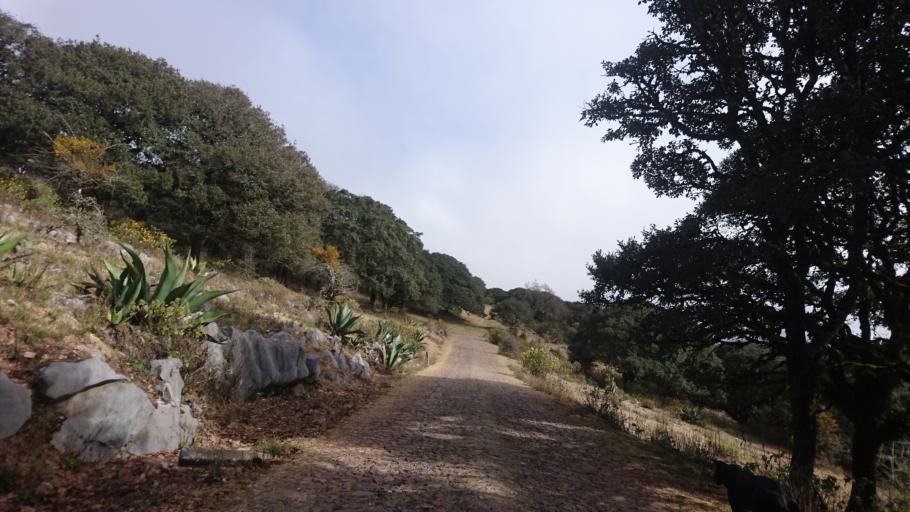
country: MX
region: San Luis Potosi
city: Zaragoza
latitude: 22.0670
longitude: -100.6443
